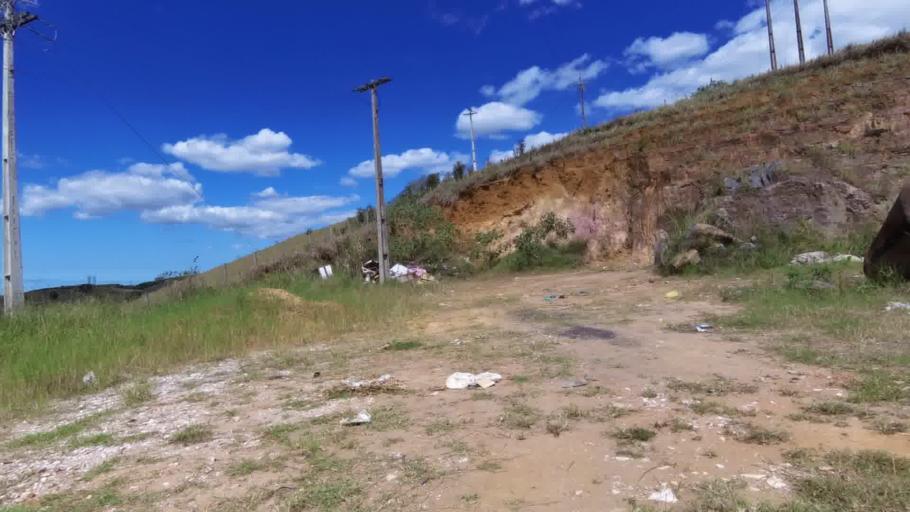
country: BR
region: Espirito Santo
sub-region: Rio Novo Do Sul
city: Rio Novo do Sul
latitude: -20.8702
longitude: -40.9387
